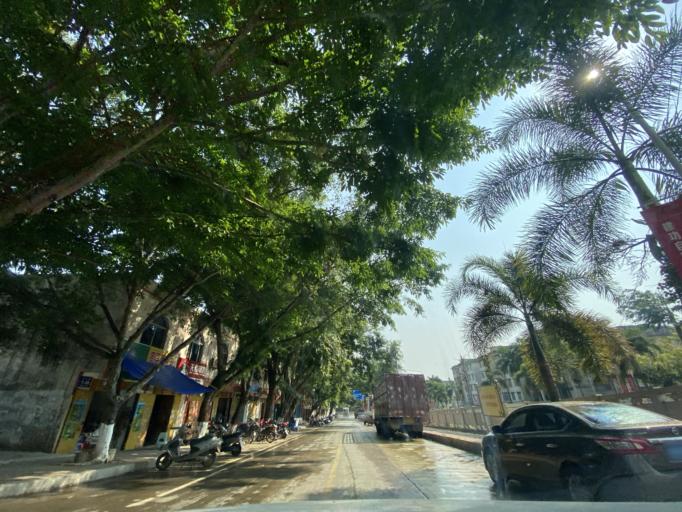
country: CN
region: Hainan
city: Chongshan
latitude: 18.7837
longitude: 109.5140
